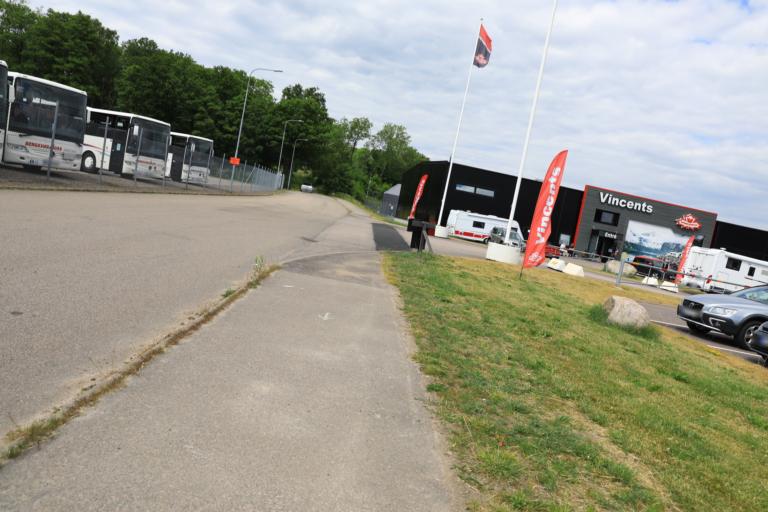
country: SE
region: Halland
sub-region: Varbergs Kommun
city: Varberg
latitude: 57.1696
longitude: 12.2760
